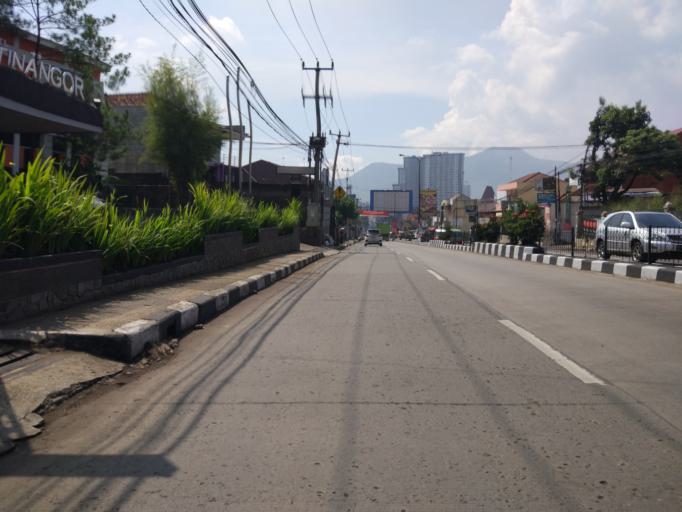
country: ID
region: West Java
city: Cileunyi
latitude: -6.9374
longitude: 107.7592
